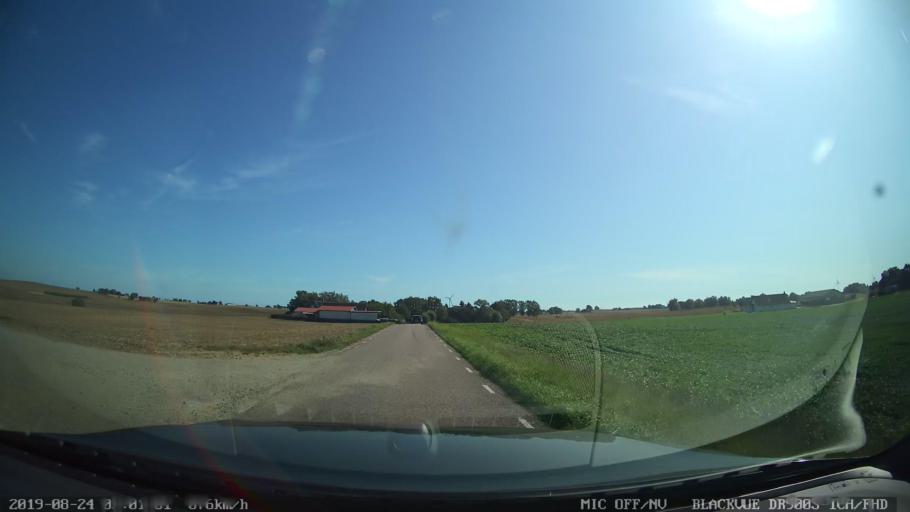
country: SE
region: Skane
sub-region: Skurups Kommun
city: Skurup
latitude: 55.4508
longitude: 13.4339
